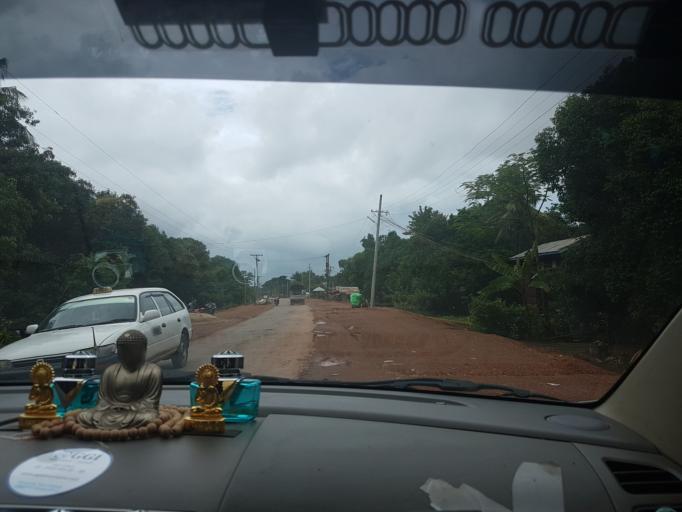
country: MM
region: Bago
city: Nyaunglebin
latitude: 17.9146
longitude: 96.8354
